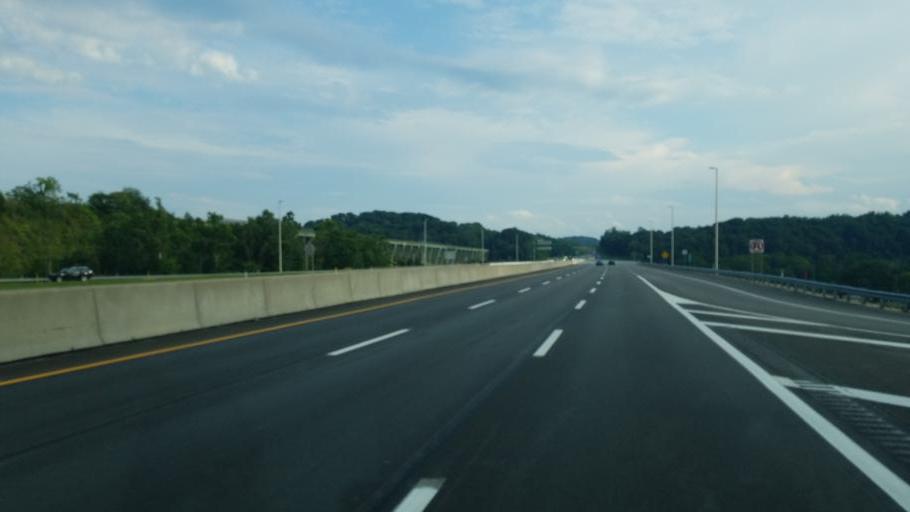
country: US
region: Pennsylvania
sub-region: Allegheny County
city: Cheswick
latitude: 40.5432
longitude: -79.8238
